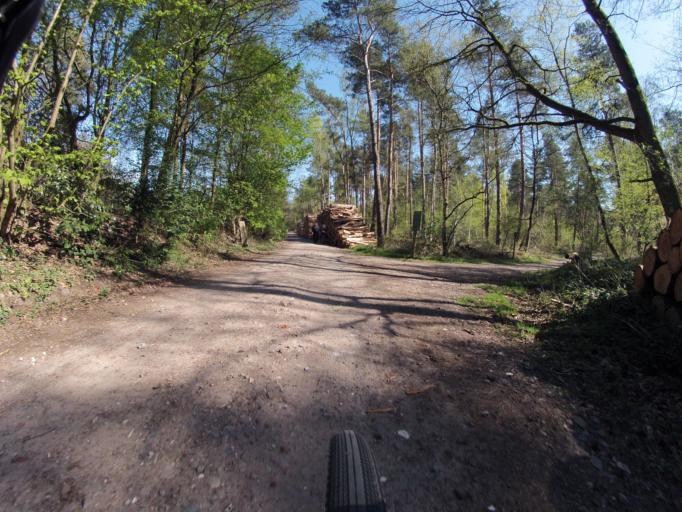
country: NL
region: Overijssel
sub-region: Gemeente Losser
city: Losser
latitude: 52.3333
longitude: 7.0293
